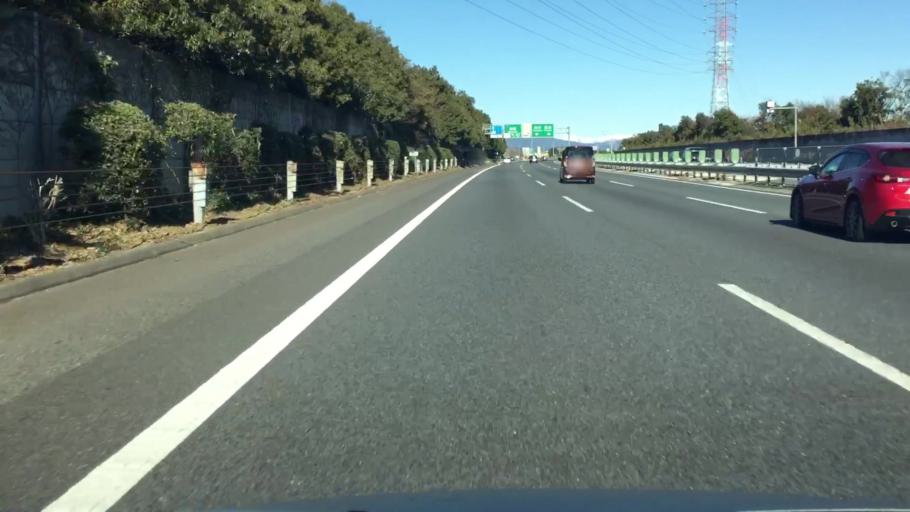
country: JP
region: Gunma
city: Maebashi-shi
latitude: 36.3693
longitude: 139.0296
